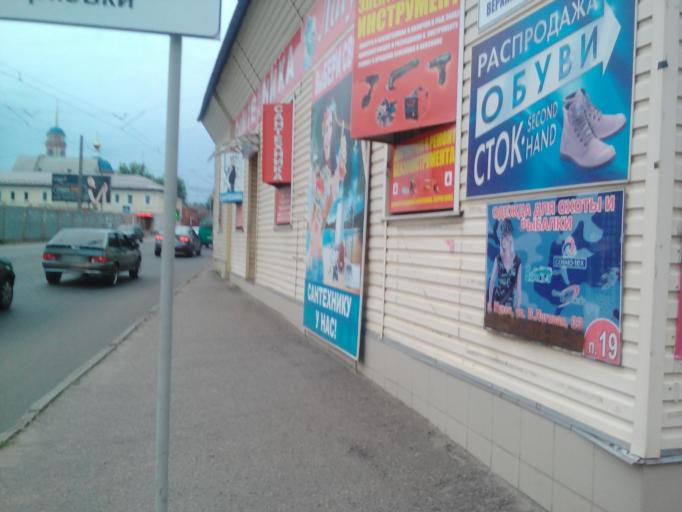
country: RU
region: Kursk
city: Kursk
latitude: 51.7305
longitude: 36.1813
